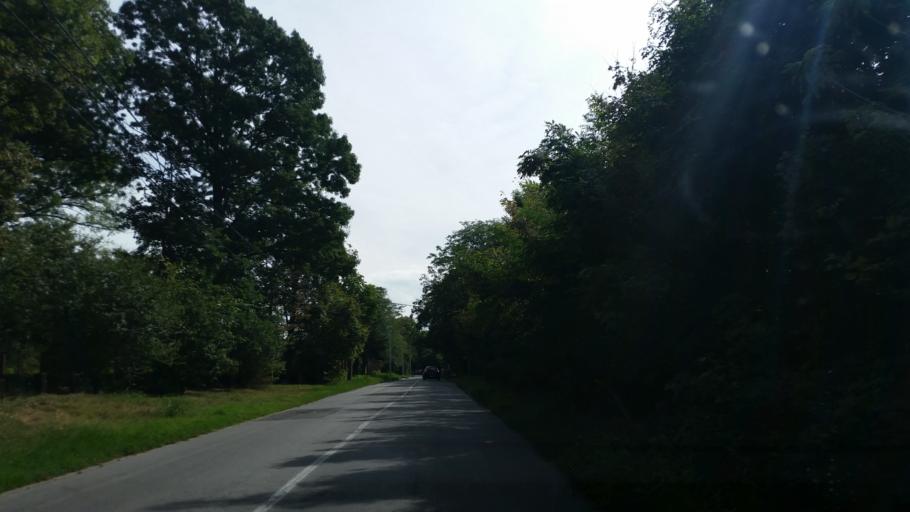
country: RS
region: Central Serbia
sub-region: Belgrade
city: Palilula
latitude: 44.8091
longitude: 20.5018
